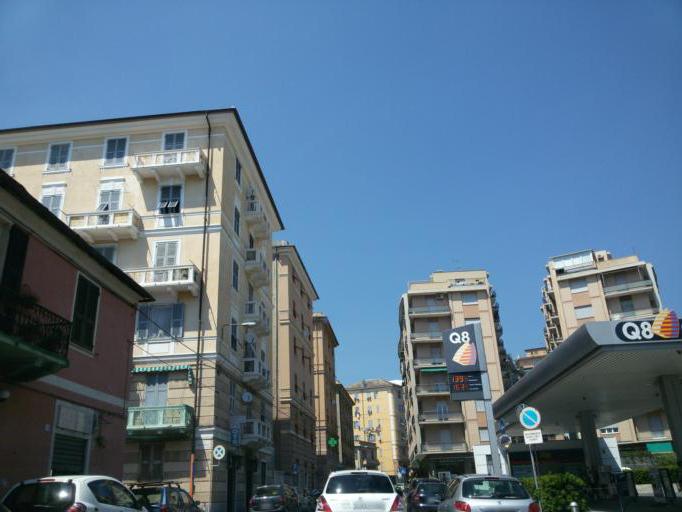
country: IT
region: Liguria
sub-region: Provincia di Genova
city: San Teodoro
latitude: 44.4247
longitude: 8.8551
